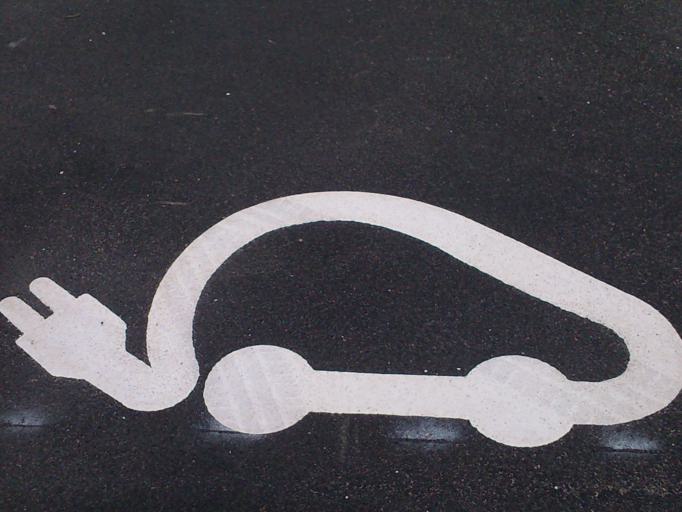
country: DK
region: Central Jutland
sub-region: Ringkobing-Skjern Kommune
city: Ringkobing
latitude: 56.0945
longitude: 8.2357
